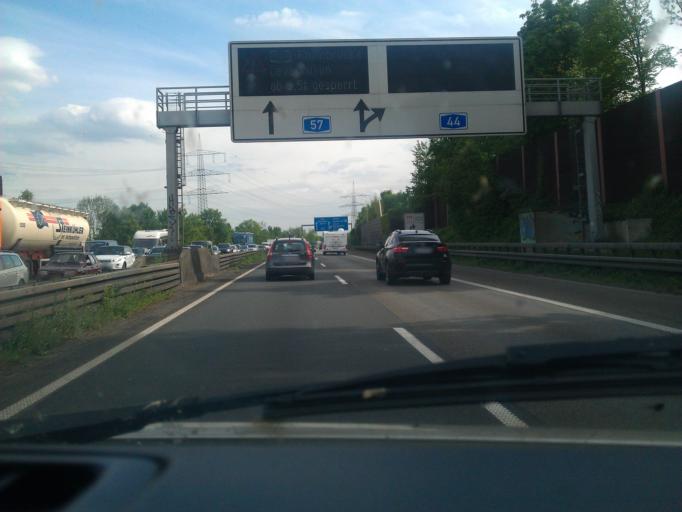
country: DE
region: North Rhine-Westphalia
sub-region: Regierungsbezirk Dusseldorf
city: Meerbusch
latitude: 51.3038
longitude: 6.6364
